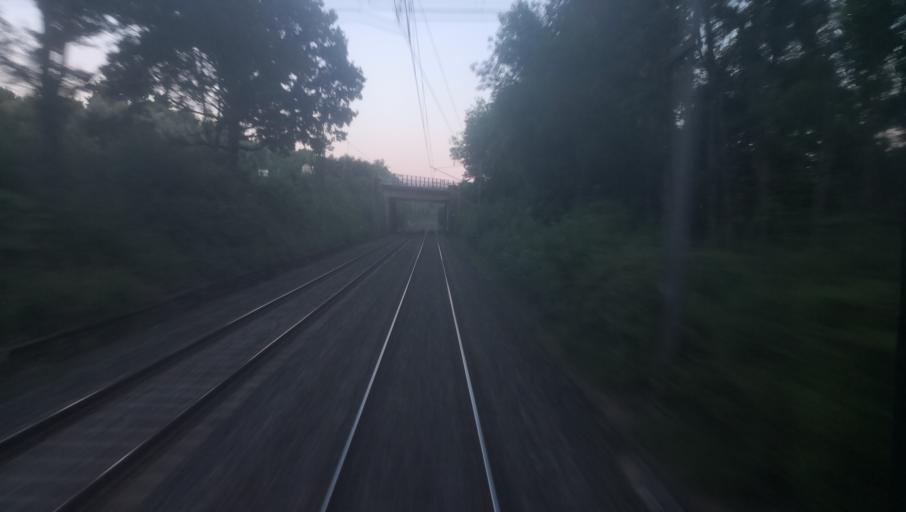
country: FR
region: Bourgogne
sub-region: Departement de la Nievre
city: Cosne-Cours-sur-Loire
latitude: 47.4432
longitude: 2.9324
